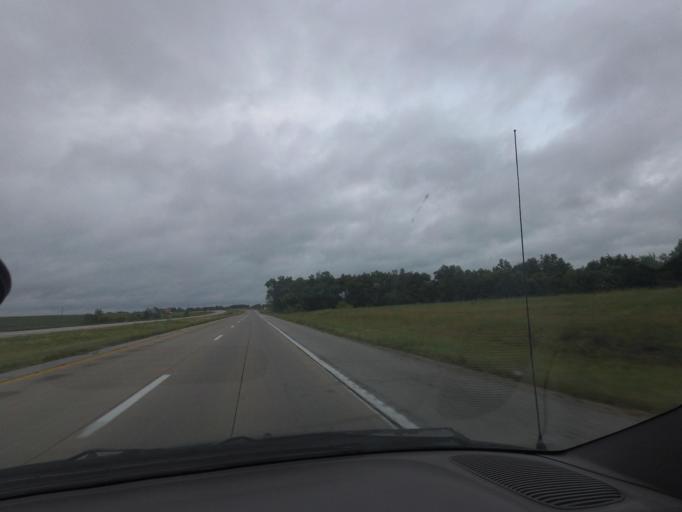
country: US
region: Missouri
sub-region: Marion County
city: Monroe City
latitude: 39.6675
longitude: -91.8515
